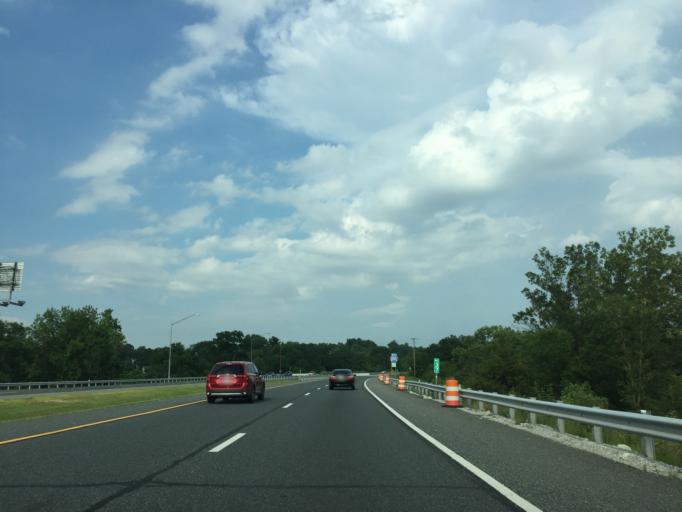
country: US
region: Maryland
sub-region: Baltimore County
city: Lansdowne
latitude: 39.2337
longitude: -76.6643
